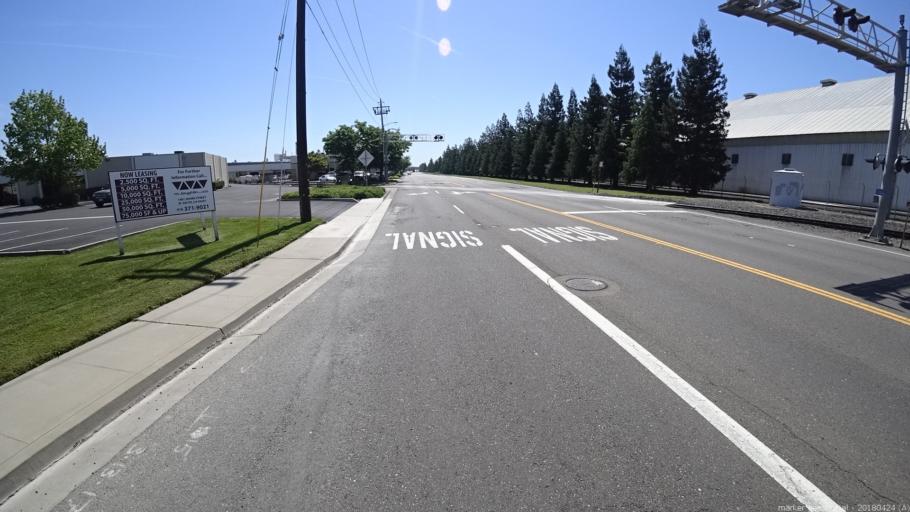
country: US
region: California
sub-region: Yolo County
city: West Sacramento
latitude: 38.5689
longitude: -121.5487
